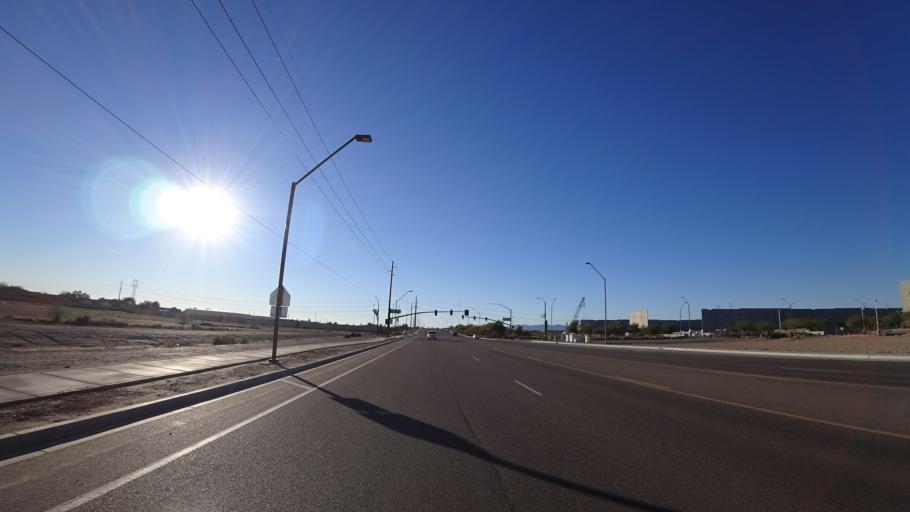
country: US
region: Arizona
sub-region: Maricopa County
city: Avondale
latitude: 33.4495
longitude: -112.3270
